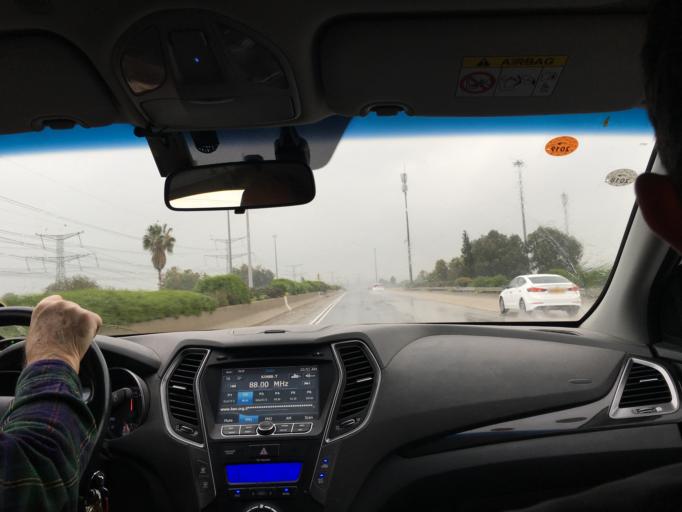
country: IL
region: Central District
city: Petah Tiqwa
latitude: 32.1217
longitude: 34.9013
